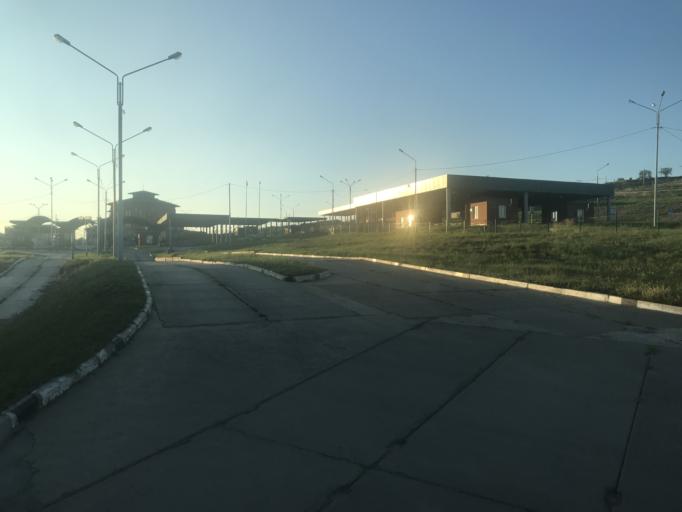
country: MN
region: Selenge
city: Altanbulag
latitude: 50.3242
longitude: 106.4888
